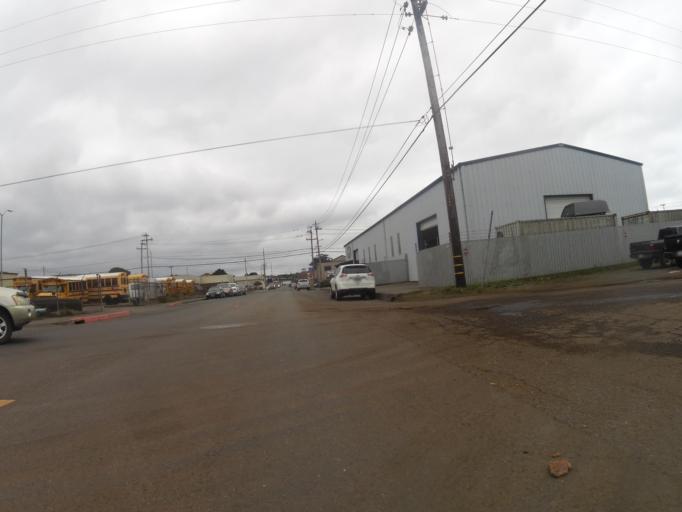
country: US
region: California
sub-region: Humboldt County
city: Eureka
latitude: 40.7949
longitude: -124.1792
